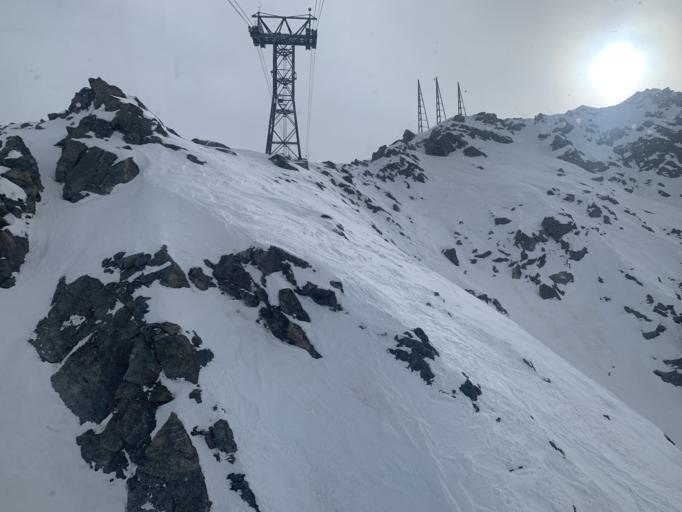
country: CH
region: Grisons
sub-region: Maloja District
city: Silvaplana
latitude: 46.4236
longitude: 9.8224
